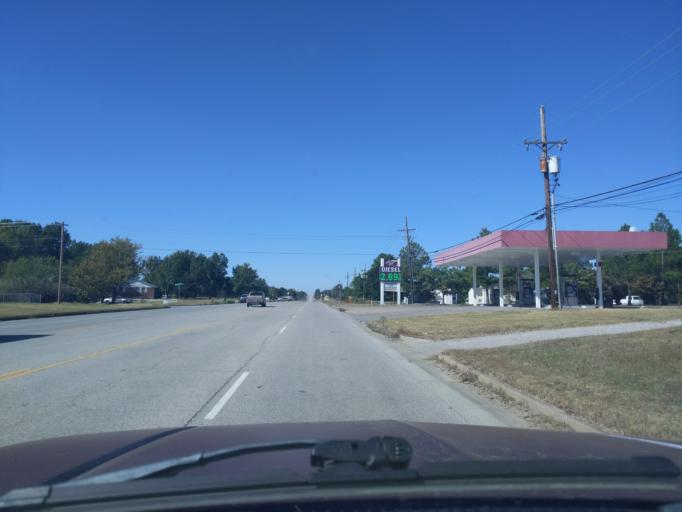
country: US
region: Oklahoma
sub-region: Creek County
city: Kiefer
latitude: 35.9885
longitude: -96.0691
